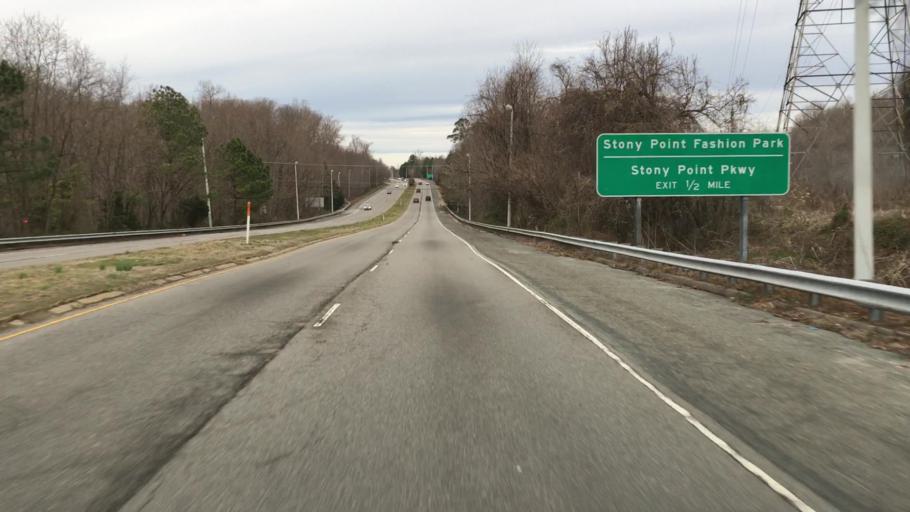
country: US
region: Virginia
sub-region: Chesterfield County
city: Bon Air
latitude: 37.5466
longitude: -77.5599
